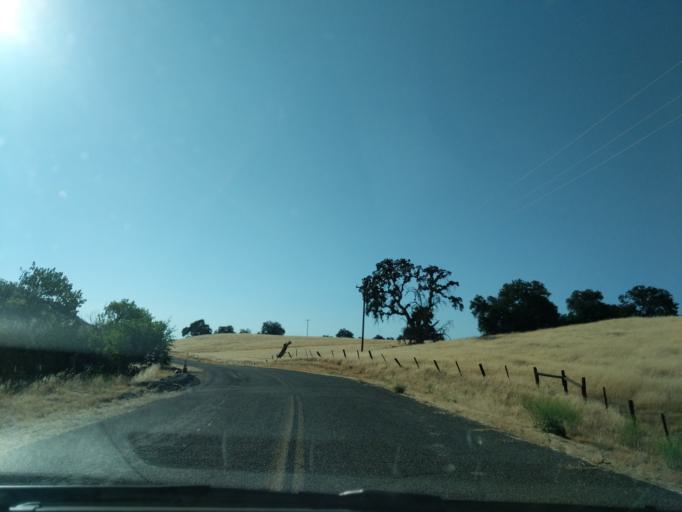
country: US
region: California
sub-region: Monterey County
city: King City
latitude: 36.1730
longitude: -120.7908
